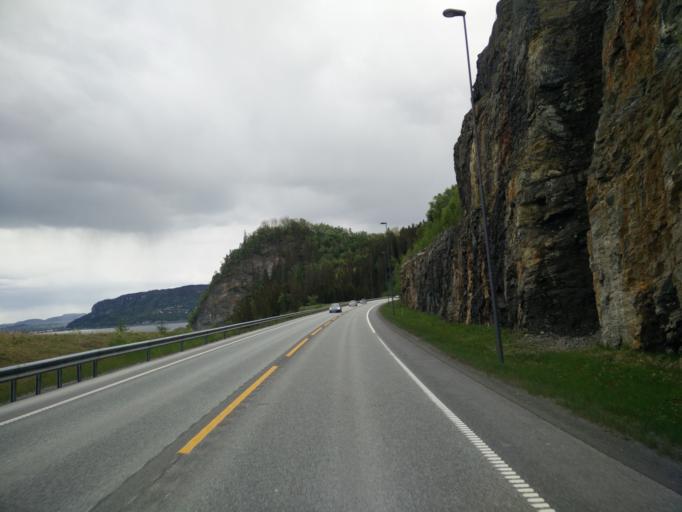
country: NO
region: Sor-Trondelag
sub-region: Skaun
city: Borsa
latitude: 63.3240
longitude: 10.1166
